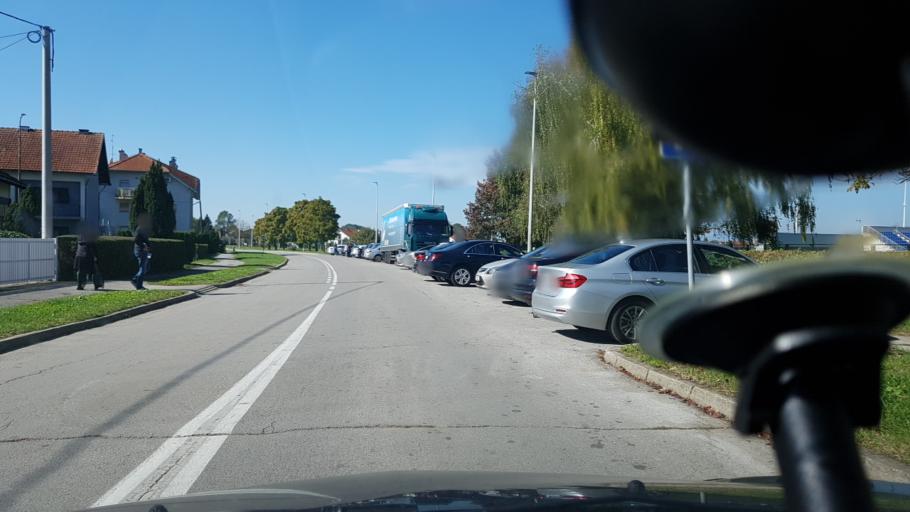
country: HR
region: Zagrebacka
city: Lupoglav
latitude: 45.7032
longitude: 16.3882
